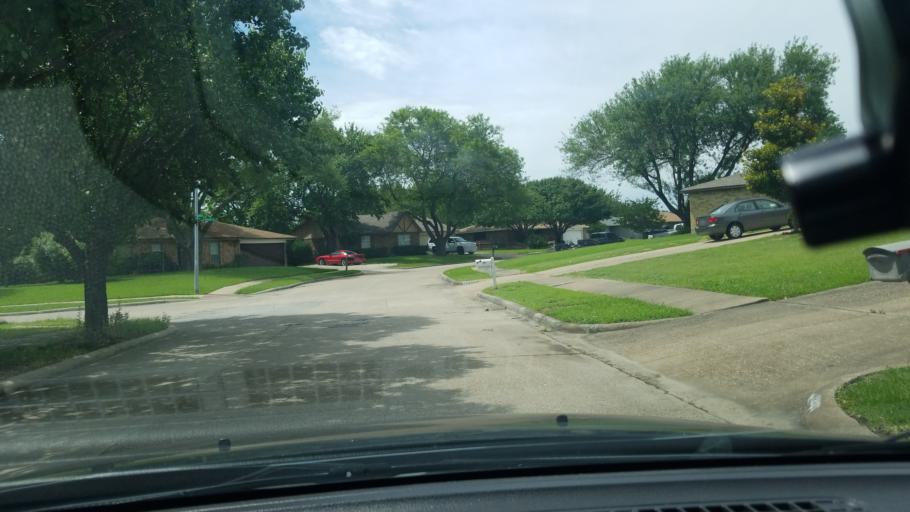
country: US
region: Texas
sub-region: Dallas County
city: Mesquite
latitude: 32.7595
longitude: -96.5765
